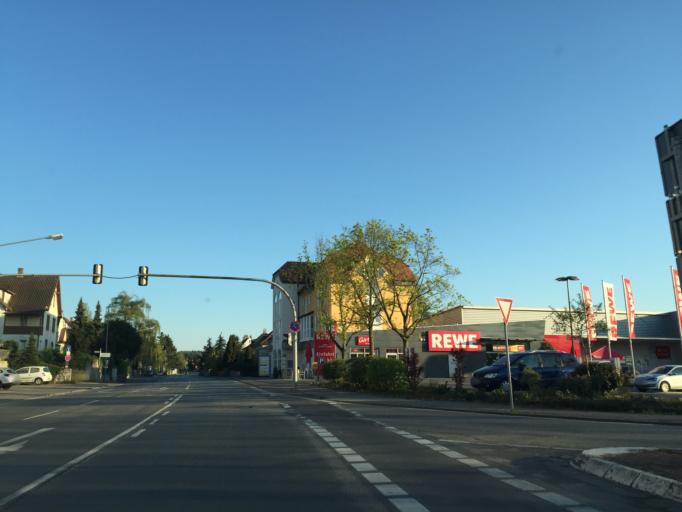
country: DE
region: Hesse
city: Zwingenberg
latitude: 49.7178
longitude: 8.6133
